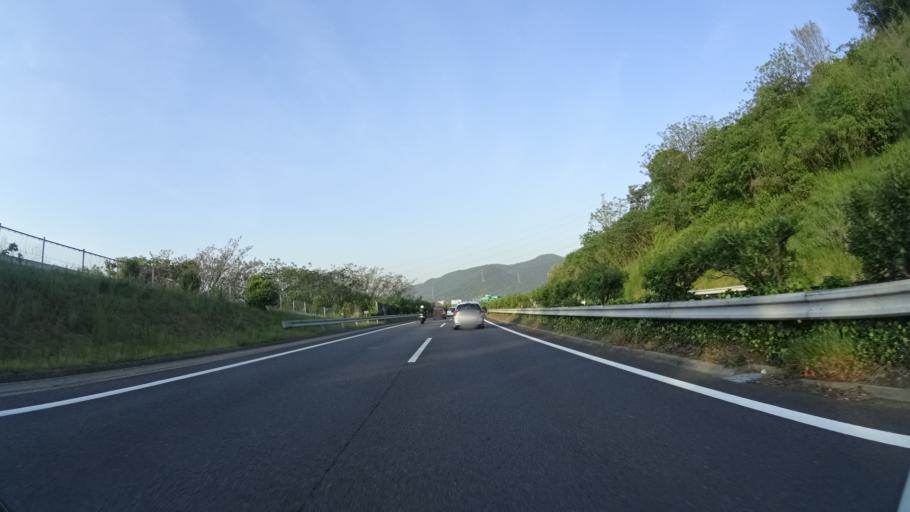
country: JP
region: Kagawa
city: Sakaidecho
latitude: 34.2809
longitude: 133.8421
